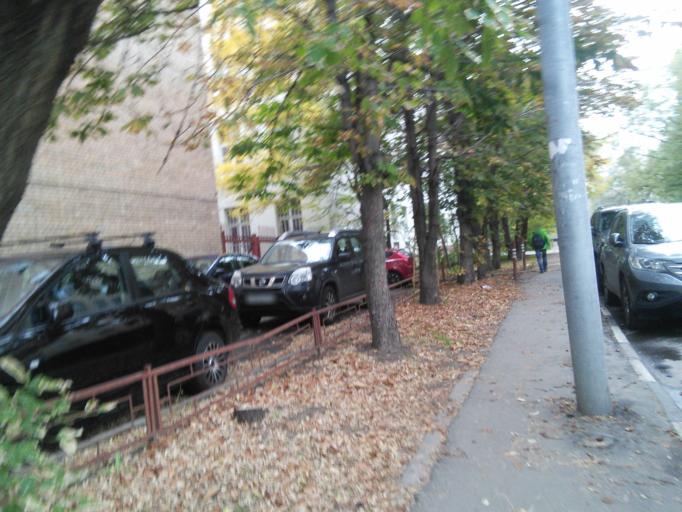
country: RU
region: Moscow
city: Novyye Cheremushki
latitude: 55.7014
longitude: 37.5752
